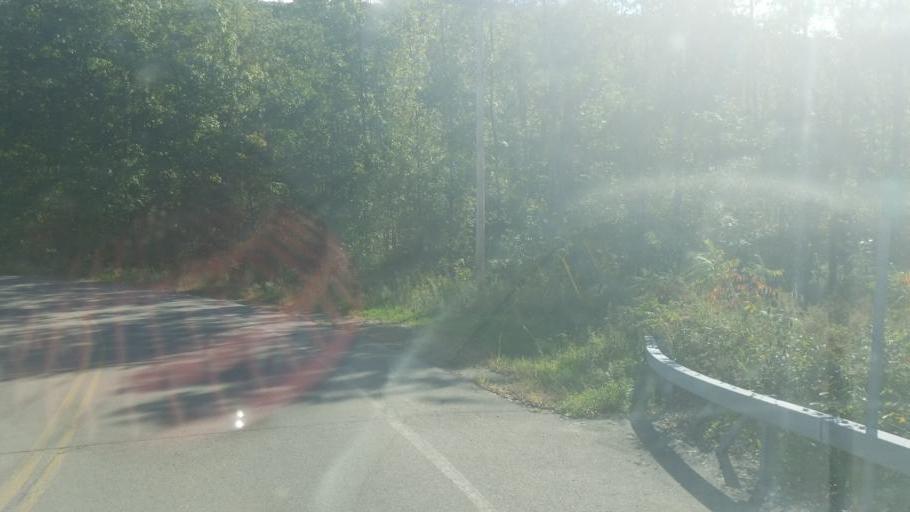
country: US
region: New York
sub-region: Allegany County
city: Cuba
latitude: 42.2363
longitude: -78.3071
